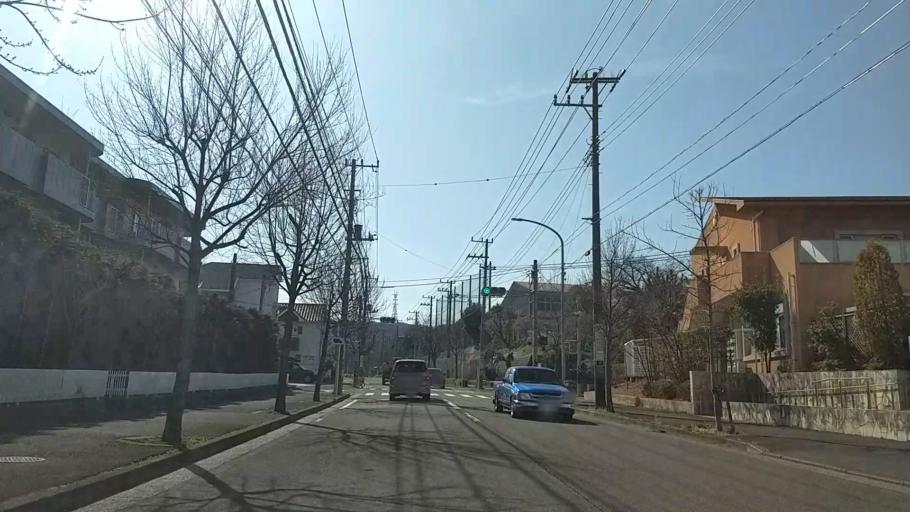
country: JP
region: Kanagawa
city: Kamakura
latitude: 35.3727
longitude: 139.5869
